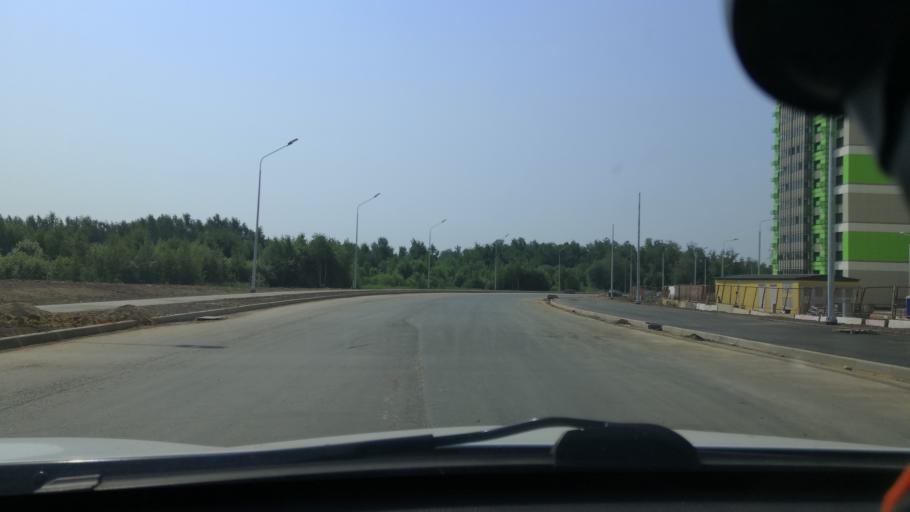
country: RU
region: Moscow
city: Severnyy
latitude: 55.9400
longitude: 37.5313
